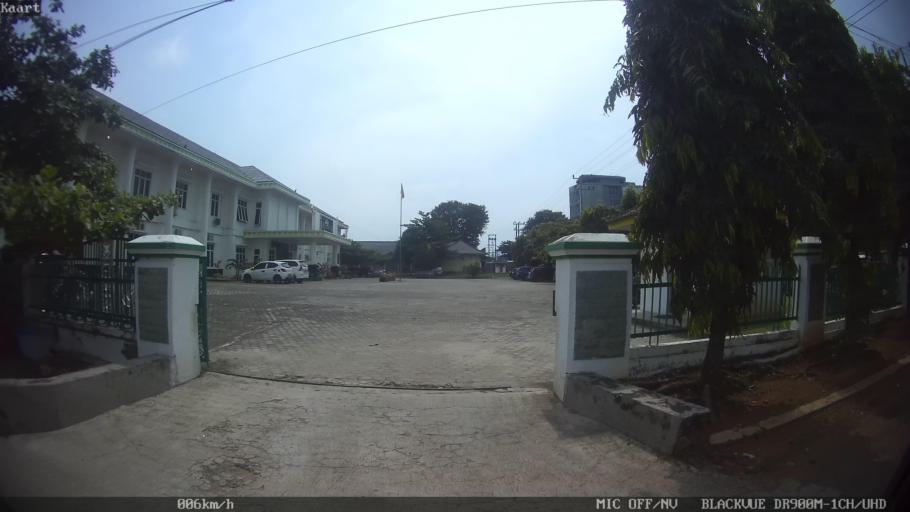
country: ID
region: Lampung
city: Bandarlampung
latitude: -5.4300
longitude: 105.2699
